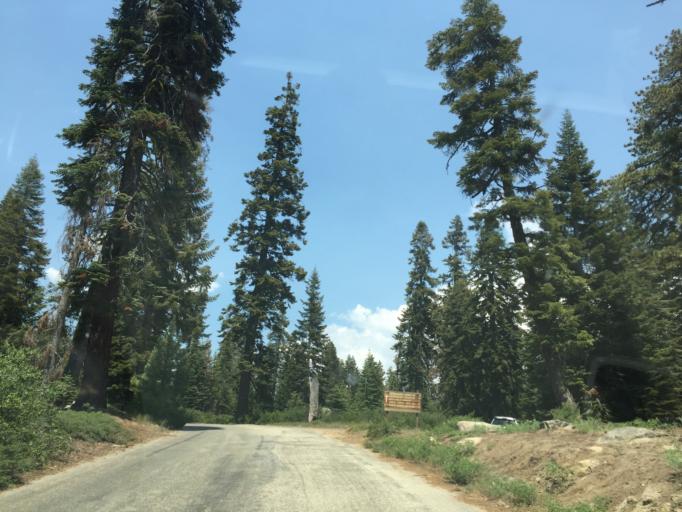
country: US
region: California
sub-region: Tulare County
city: Three Rivers
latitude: 36.7001
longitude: -118.8756
